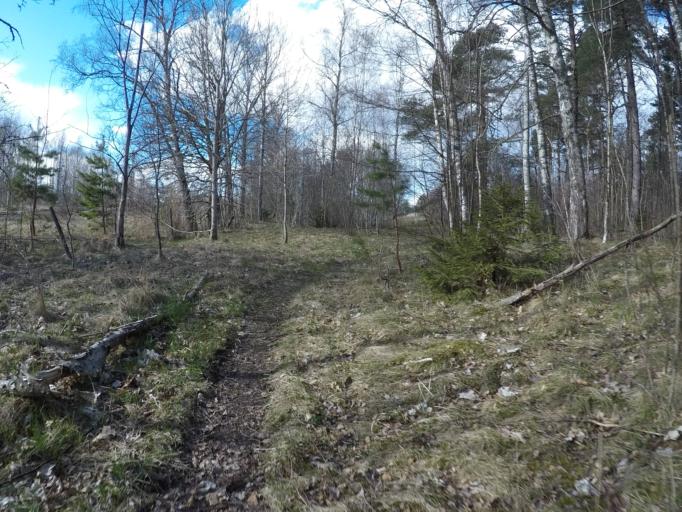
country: SE
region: Vaestmanland
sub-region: Hallstahammars Kommun
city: Kolback
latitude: 59.5011
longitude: 16.2681
